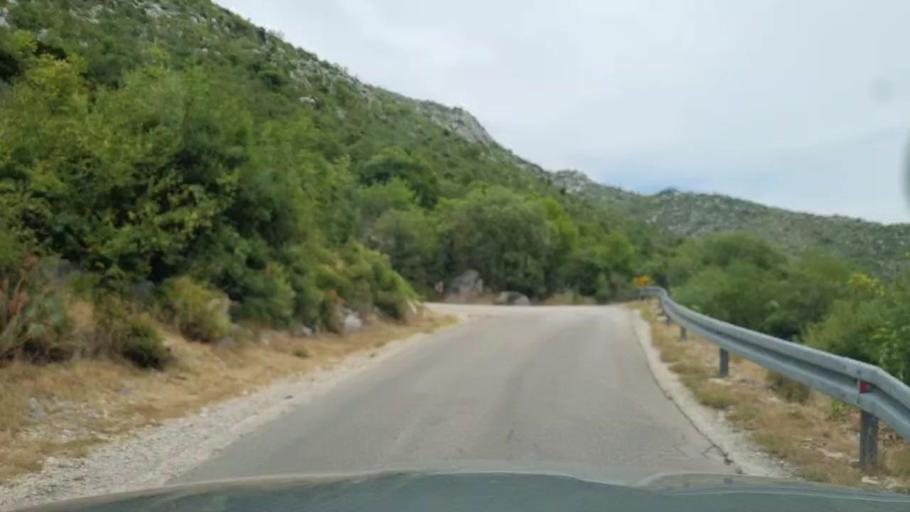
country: HR
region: Dubrovacko-Neretvanska
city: Podgora
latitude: 42.9666
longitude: 17.7957
